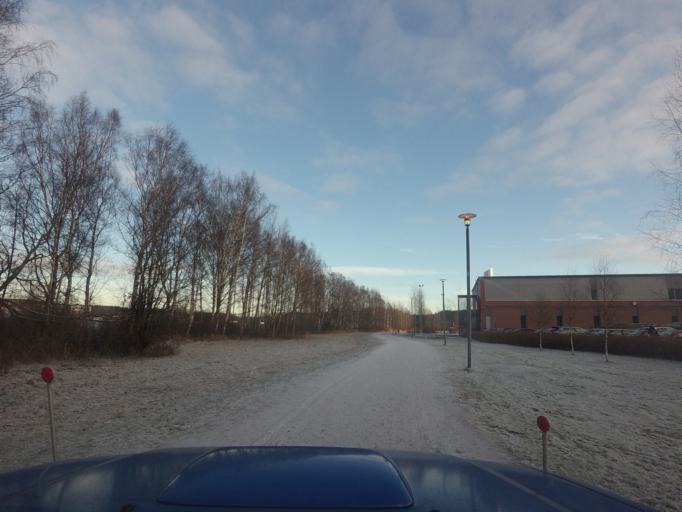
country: FI
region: Uusimaa
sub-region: Helsinki
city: Espoo
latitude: 60.2107
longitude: 24.6580
